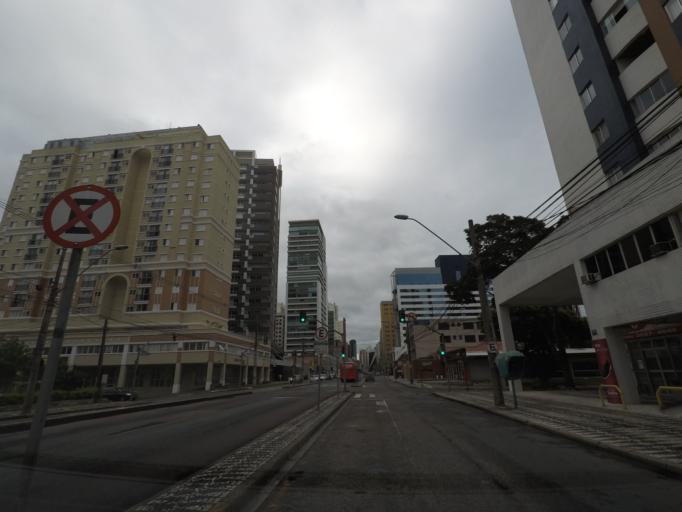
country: BR
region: Parana
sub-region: Curitiba
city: Curitiba
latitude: -25.4591
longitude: -49.2889
